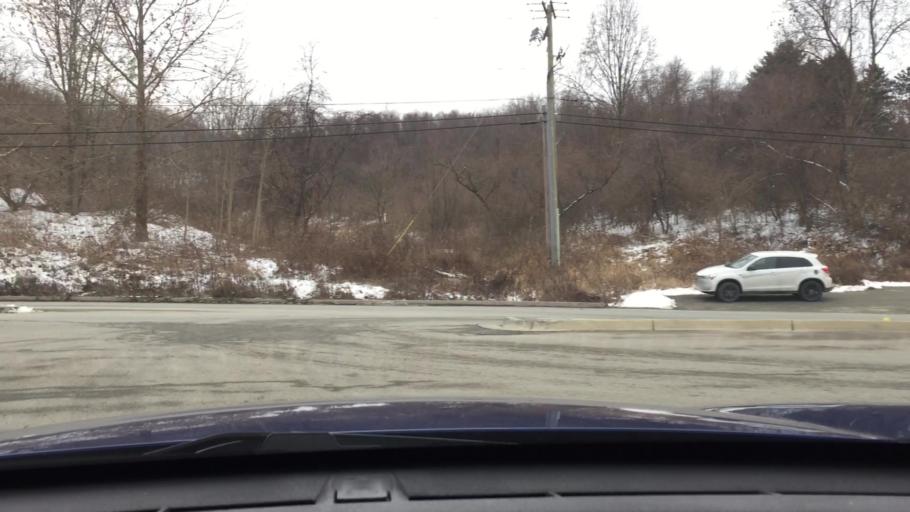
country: US
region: Pennsylvania
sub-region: Washington County
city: McGovern
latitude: 40.2116
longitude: -80.1951
